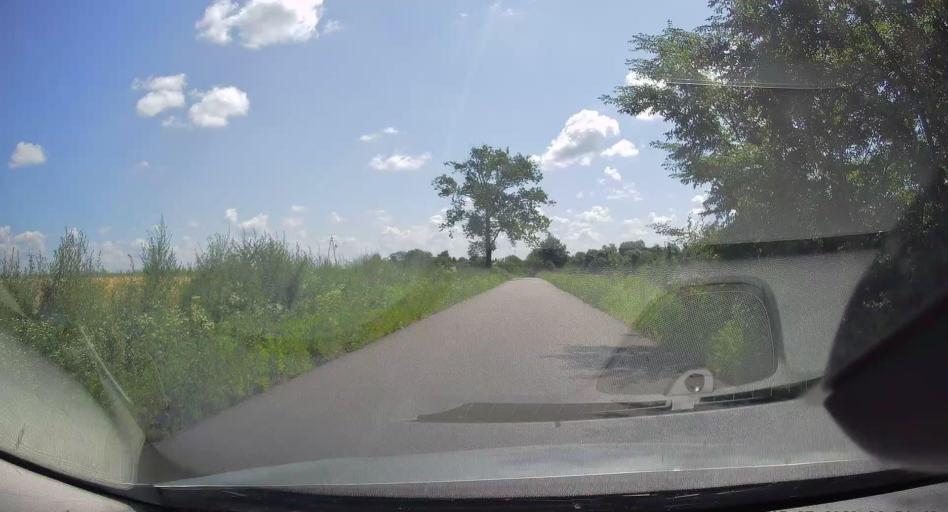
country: PL
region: Subcarpathian Voivodeship
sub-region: Powiat jaroslawski
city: Sosnica
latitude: 49.8667
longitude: 22.8663
